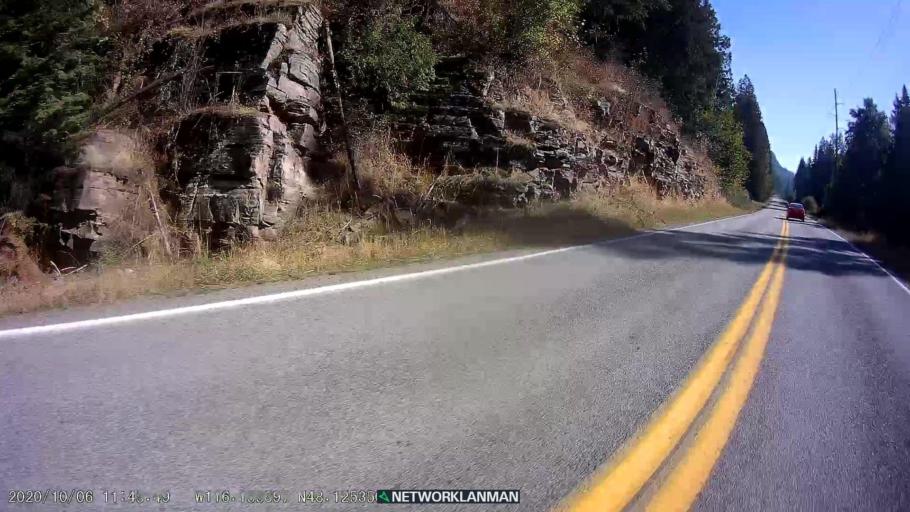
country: US
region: Idaho
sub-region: Bonner County
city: Ponderay
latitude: 48.1255
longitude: -116.1557
